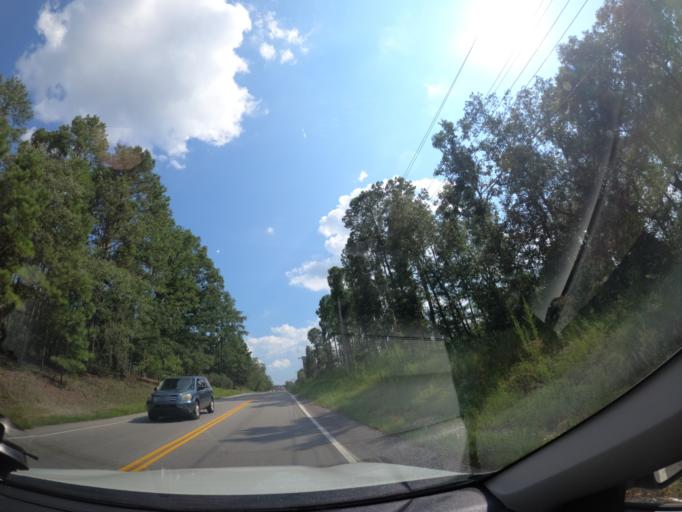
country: US
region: South Carolina
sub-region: Lexington County
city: South Congaree
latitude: 33.9068
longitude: -81.1614
